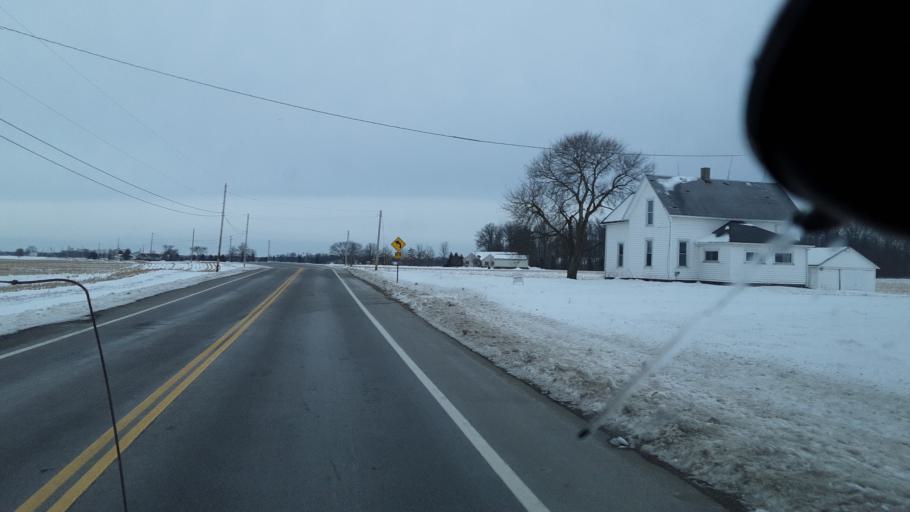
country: US
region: Ohio
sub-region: Union County
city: Marysville
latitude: 40.1853
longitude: -83.3378
